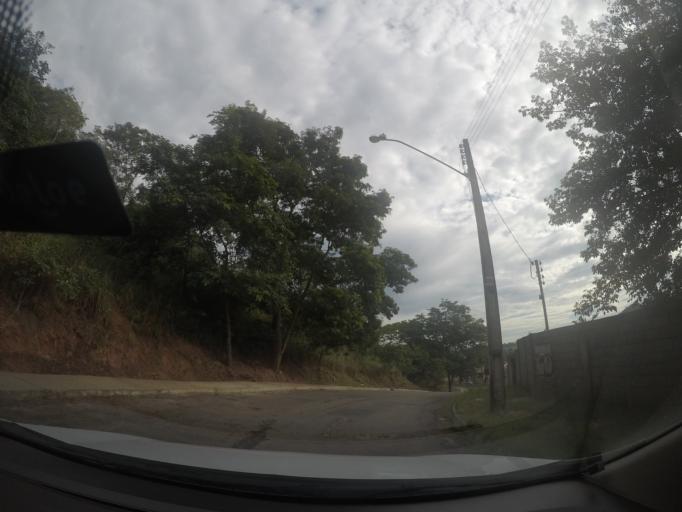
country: BR
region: Goias
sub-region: Goiania
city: Goiania
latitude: -16.6869
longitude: -49.2008
